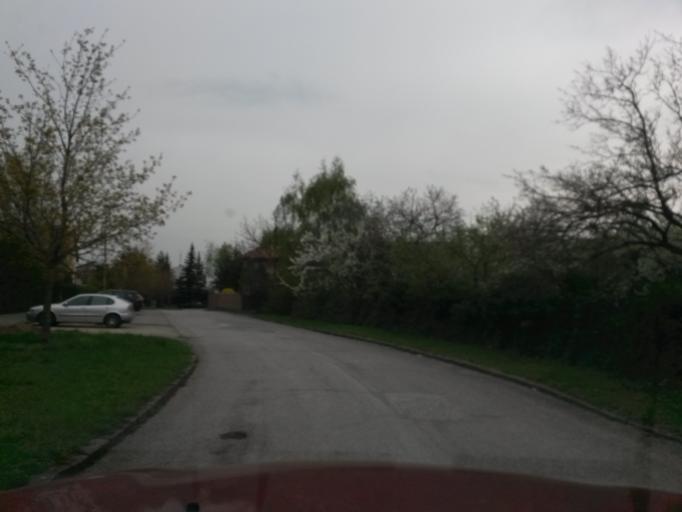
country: SK
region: Kosicky
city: Kosice
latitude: 48.7071
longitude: 21.2278
